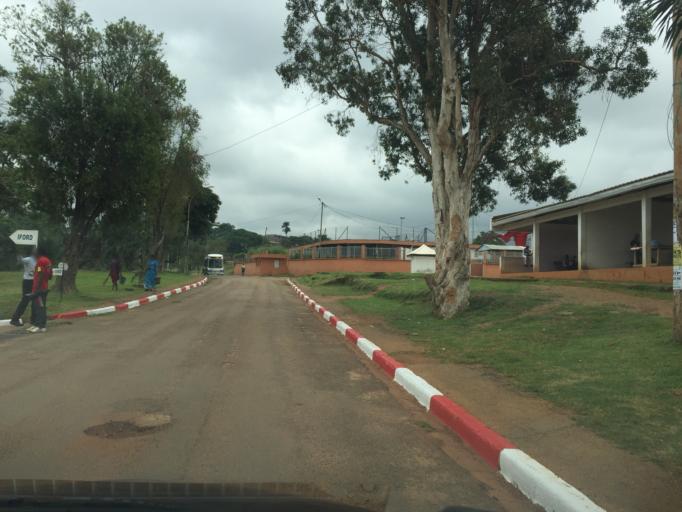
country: CM
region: Centre
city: Yaounde
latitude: 3.8585
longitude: 11.4969
